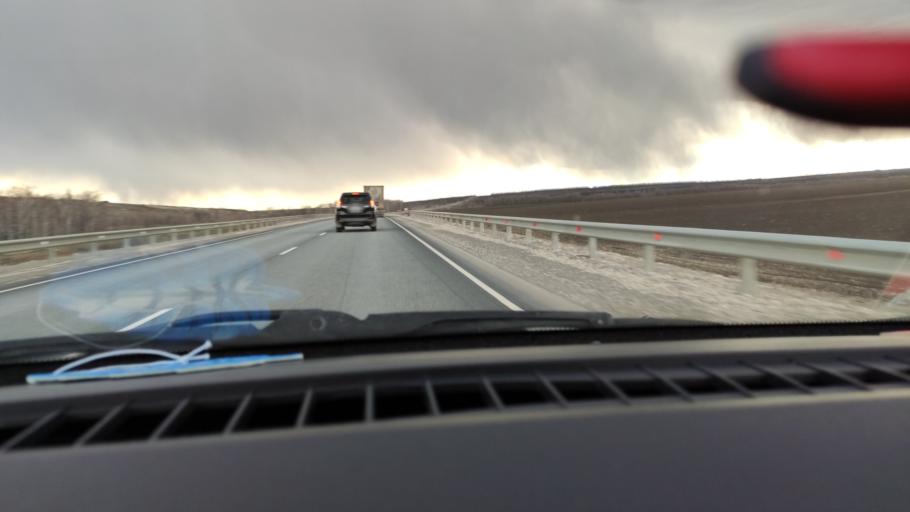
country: RU
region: Saratov
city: Yelshanka
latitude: 51.8570
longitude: 46.4951
